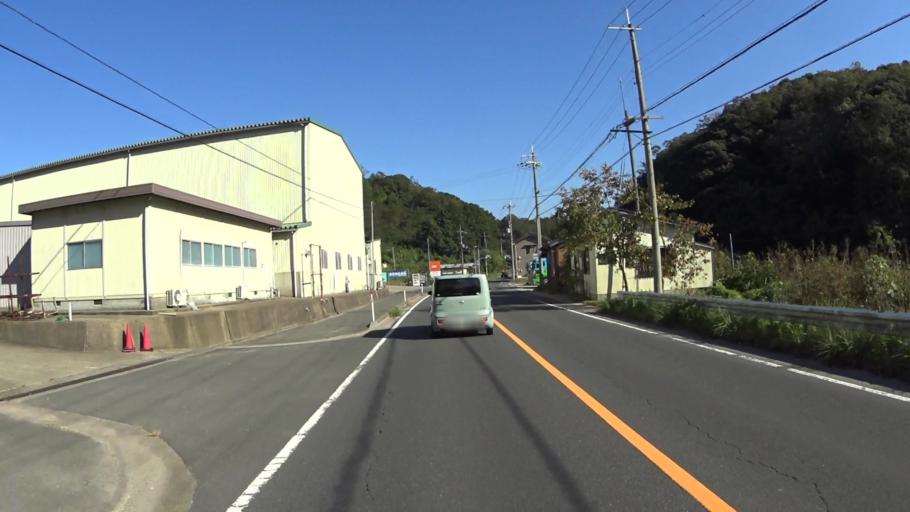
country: JP
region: Kyoto
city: Miyazu
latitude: 35.6499
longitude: 135.0389
